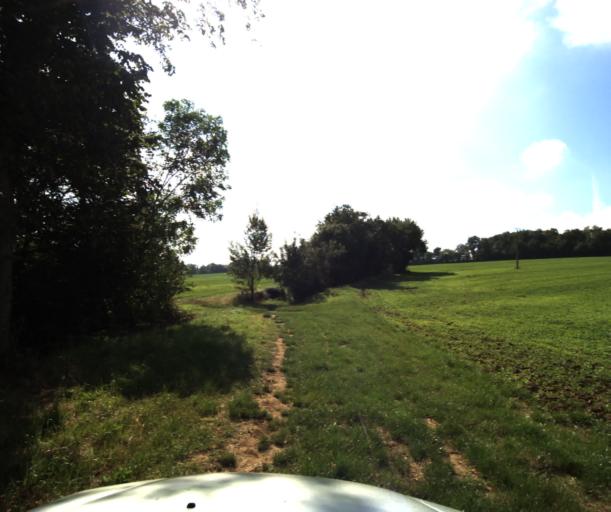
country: FR
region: Midi-Pyrenees
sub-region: Departement de la Haute-Garonne
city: Vieille-Toulouse
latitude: 43.5167
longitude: 1.4282
